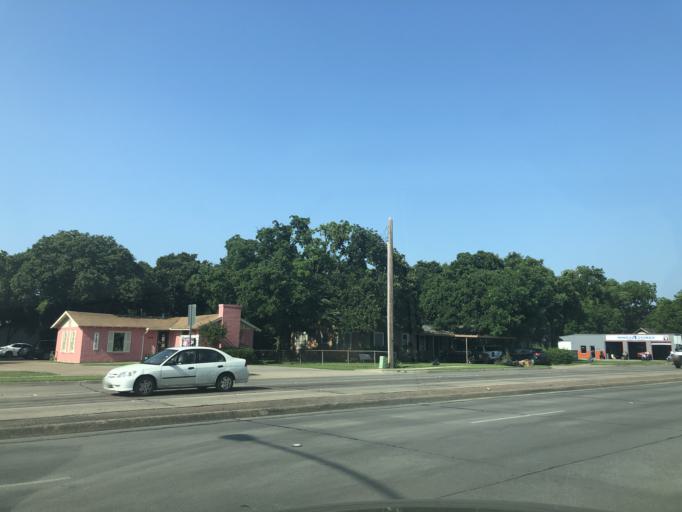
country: US
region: Texas
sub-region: Dallas County
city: Irving
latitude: 32.8088
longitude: -96.9601
